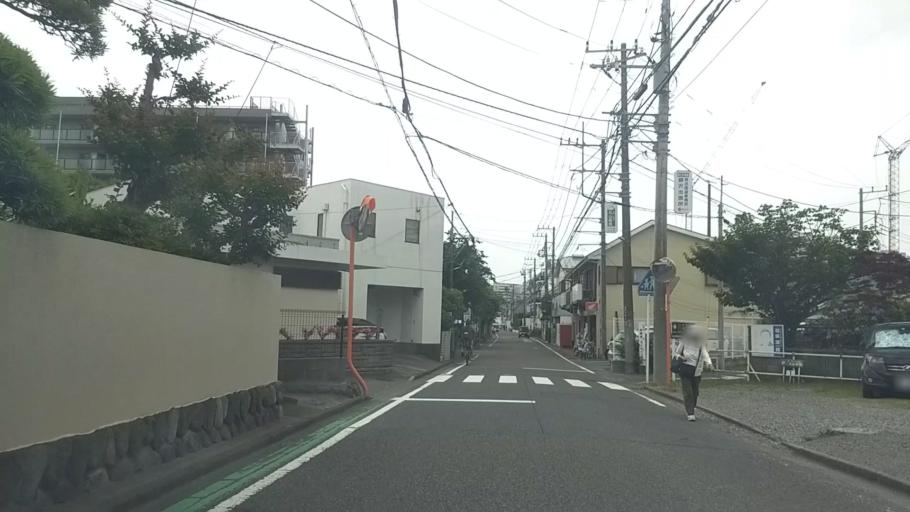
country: JP
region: Kanagawa
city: Fujisawa
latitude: 35.3433
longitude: 139.4549
